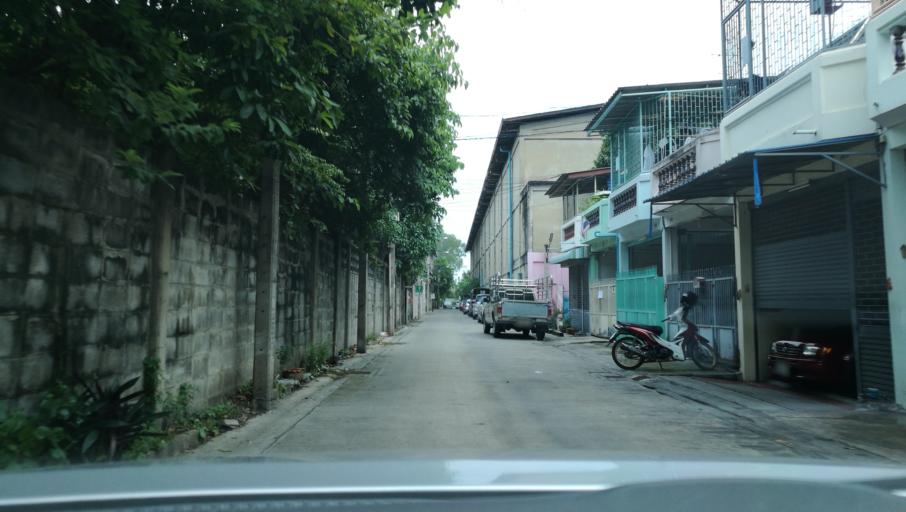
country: TH
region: Bangkok
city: Bang Sue
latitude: 13.8123
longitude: 100.5330
